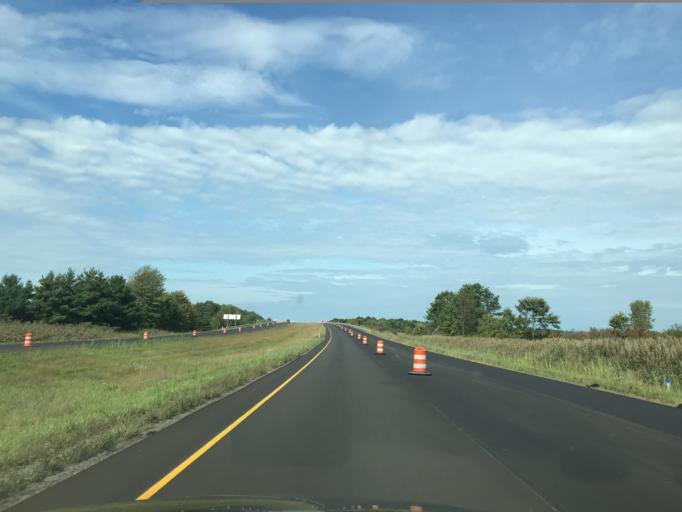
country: US
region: Ohio
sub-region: Ashtabula County
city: Jefferson
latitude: 41.7968
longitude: -80.7439
